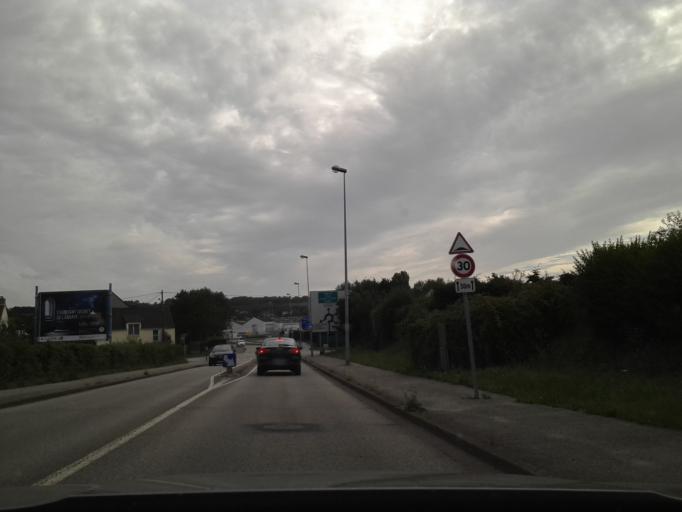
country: FR
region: Lower Normandy
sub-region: Departement de la Manche
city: Tourlaville
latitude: 49.6380
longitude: -1.5743
